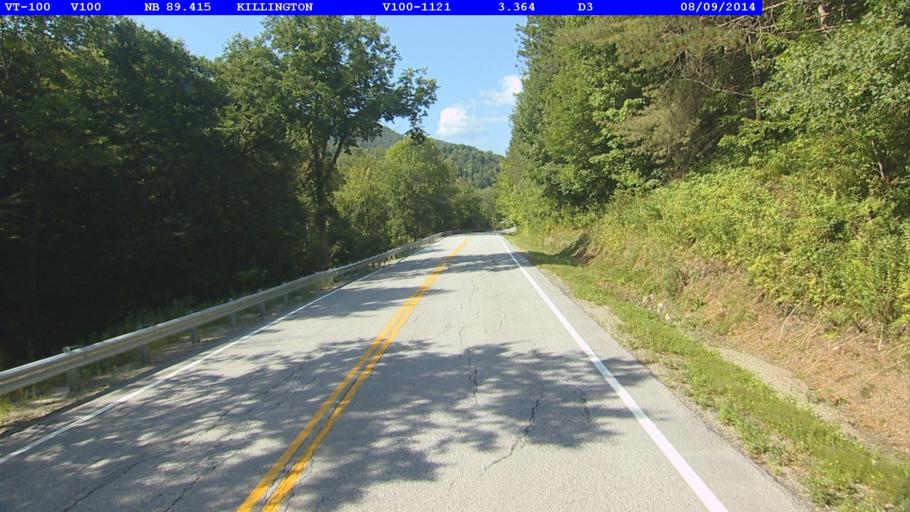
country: US
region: Vermont
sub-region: Rutland County
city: Rutland
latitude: 43.7097
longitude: -72.8261
